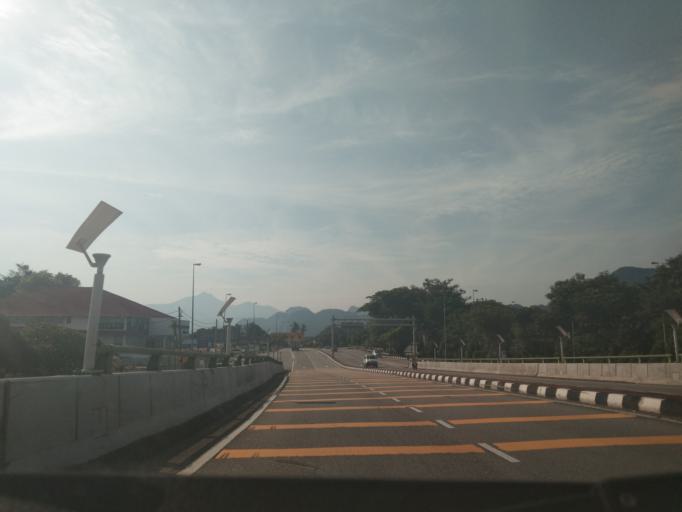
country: MY
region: Perak
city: Ipoh
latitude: 4.5771
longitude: 101.1075
